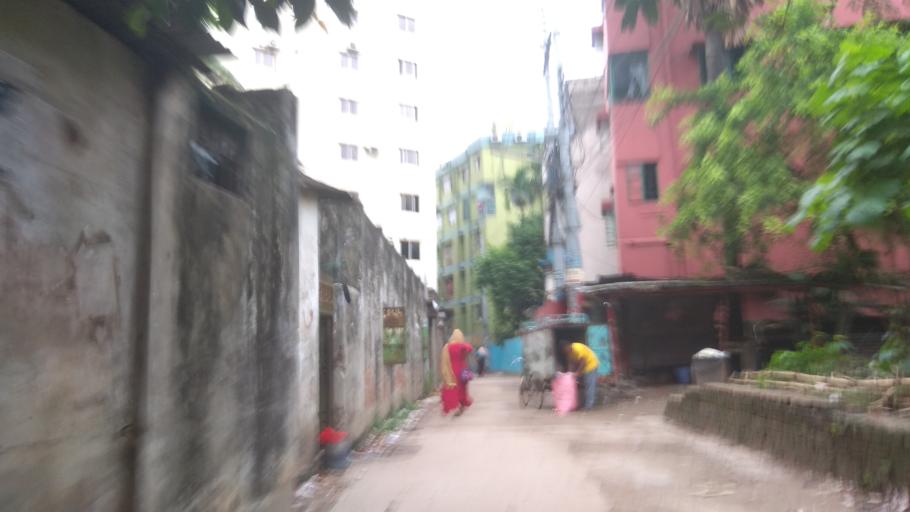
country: BD
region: Dhaka
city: Azimpur
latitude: 23.8044
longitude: 90.3740
